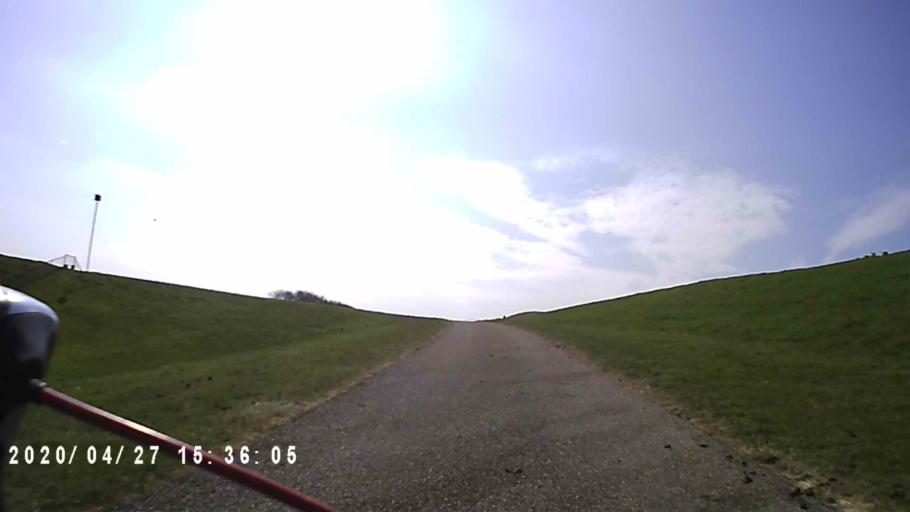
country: NL
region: Groningen
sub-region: Gemeente De Marne
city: Ulrum
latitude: 53.3977
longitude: 6.3293
